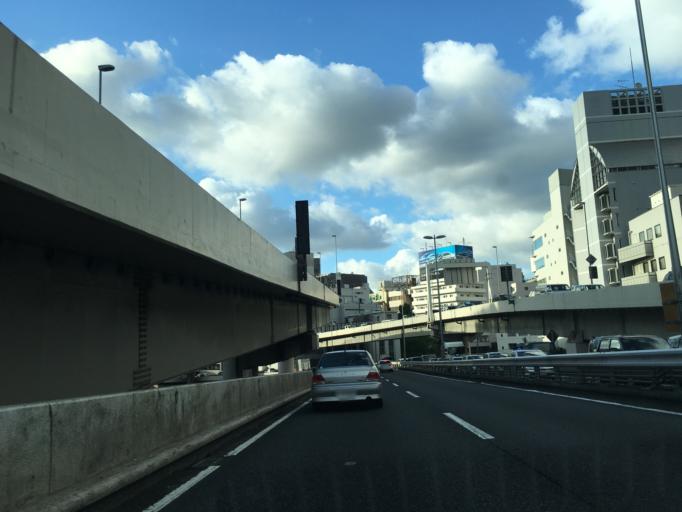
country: JP
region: Tokyo
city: Tokyo
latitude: 35.6825
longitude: 139.7800
